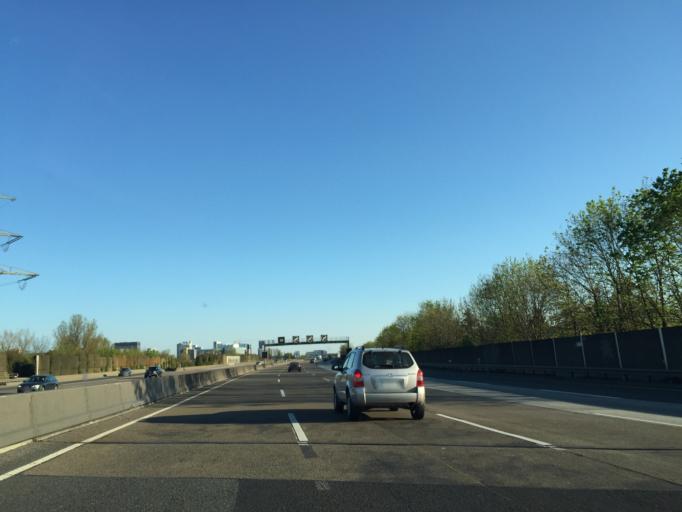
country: DE
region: Hesse
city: Niederrad
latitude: 50.0939
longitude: 8.6162
